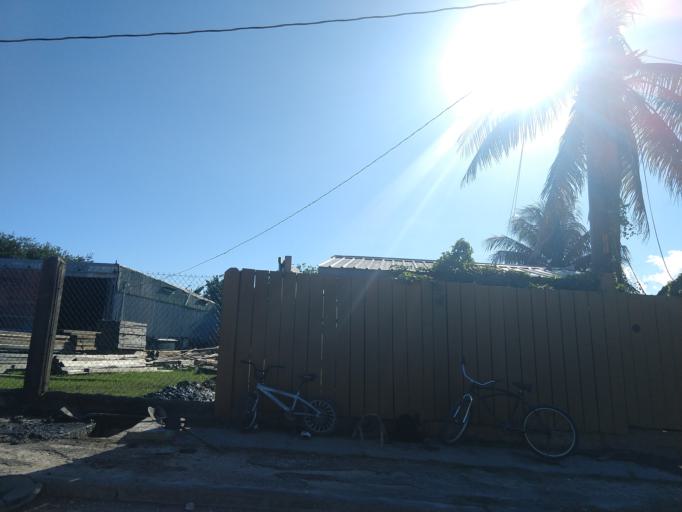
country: BZ
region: Belize
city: Belize City
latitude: 17.5052
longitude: -88.2003
